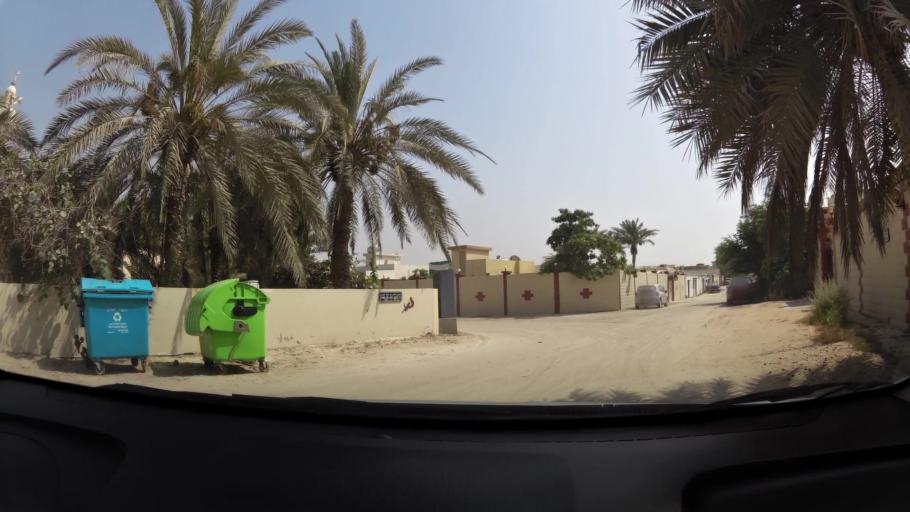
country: AE
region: Ajman
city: Ajman
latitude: 25.3860
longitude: 55.4194
